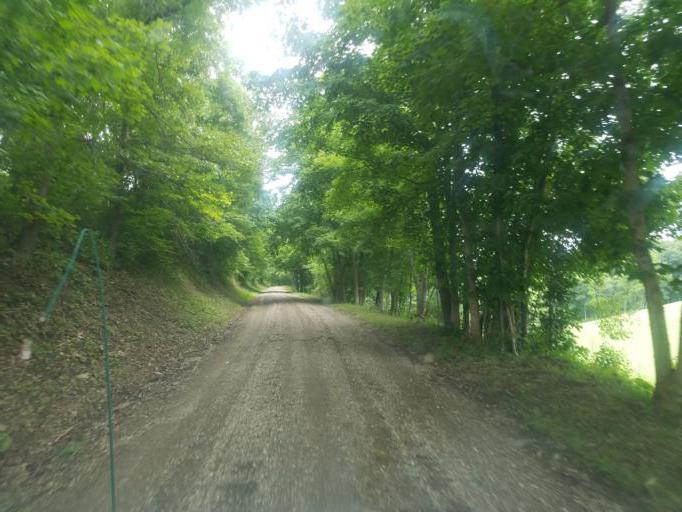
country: US
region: Ohio
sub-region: Knox County
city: Oak Hill
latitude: 40.3130
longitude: -82.1009
